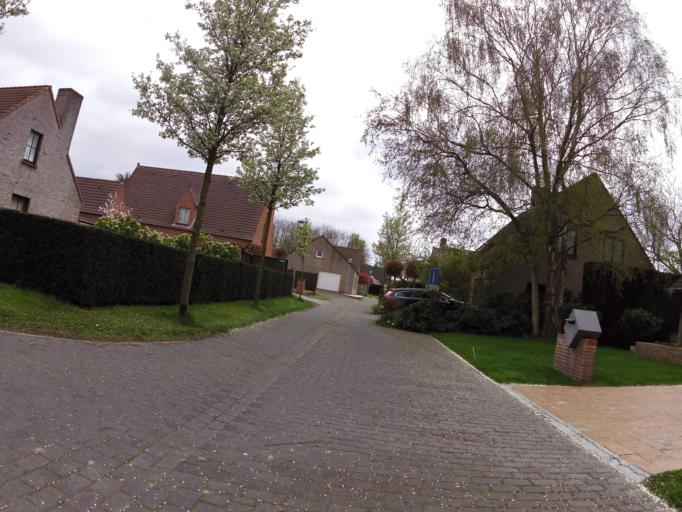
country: BE
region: Flanders
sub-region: Provincie West-Vlaanderen
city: Jabbeke
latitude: 51.1905
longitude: 3.1343
